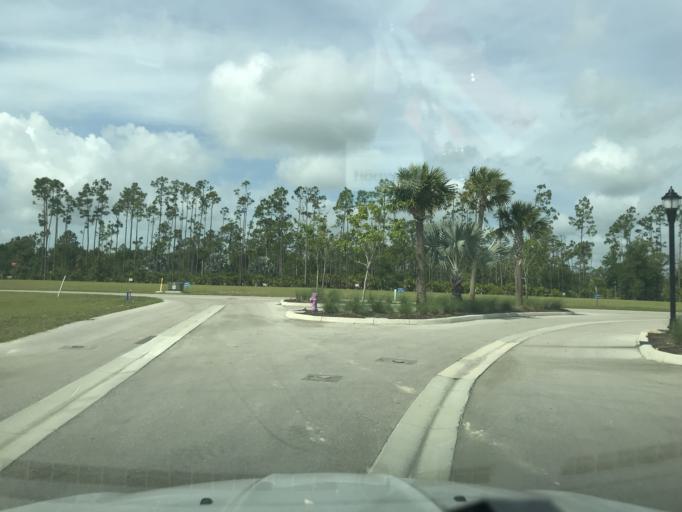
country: US
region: Florida
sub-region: Lee County
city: Fort Myers Shores
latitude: 26.7846
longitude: -81.7531
